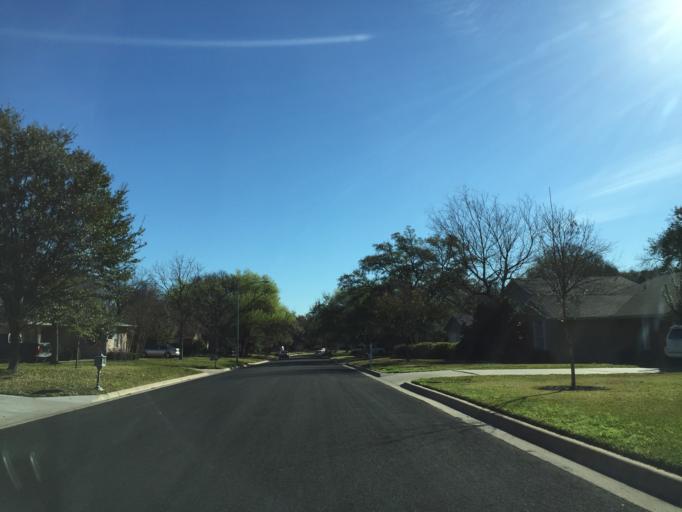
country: US
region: Texas
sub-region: Williamson County
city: Jollyville
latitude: 30.4045
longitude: -97.7351
